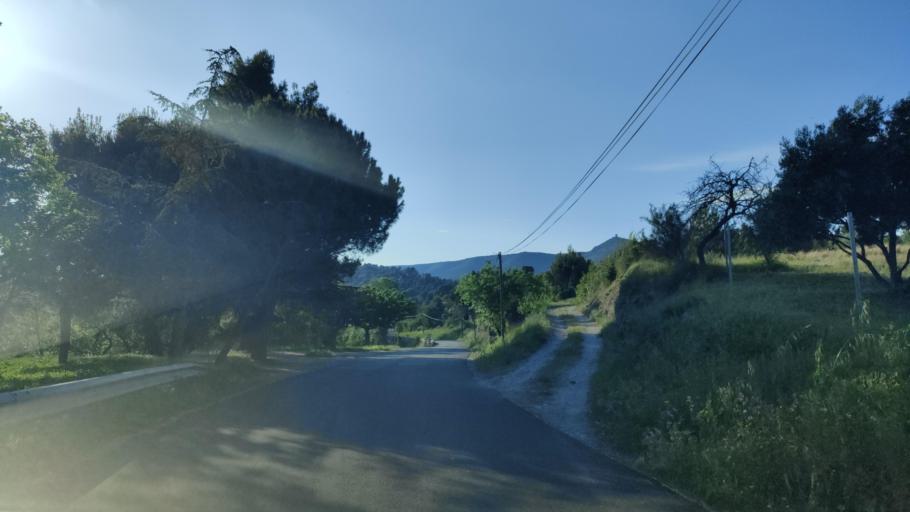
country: FR
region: Languedoc-Roussillon
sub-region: Departement des Pyrenees-Orientales
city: Baixas
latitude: 42.7813
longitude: 2.7811
